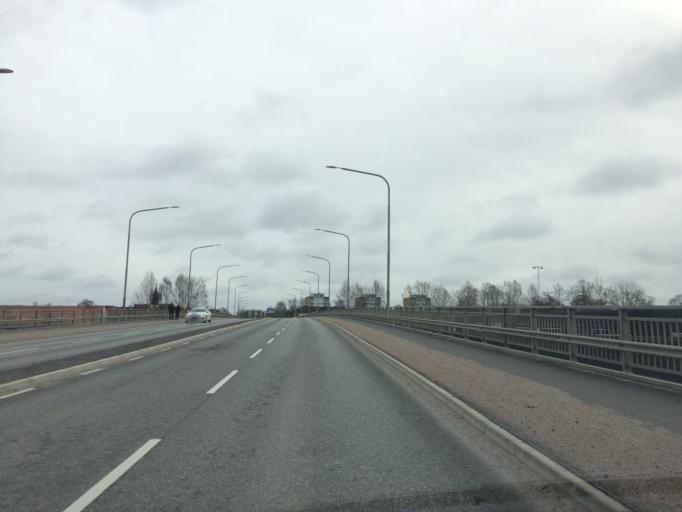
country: SE
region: Kronoberg
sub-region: Almhults Kommun
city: AElmhult
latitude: 56.5504
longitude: 14.1334
